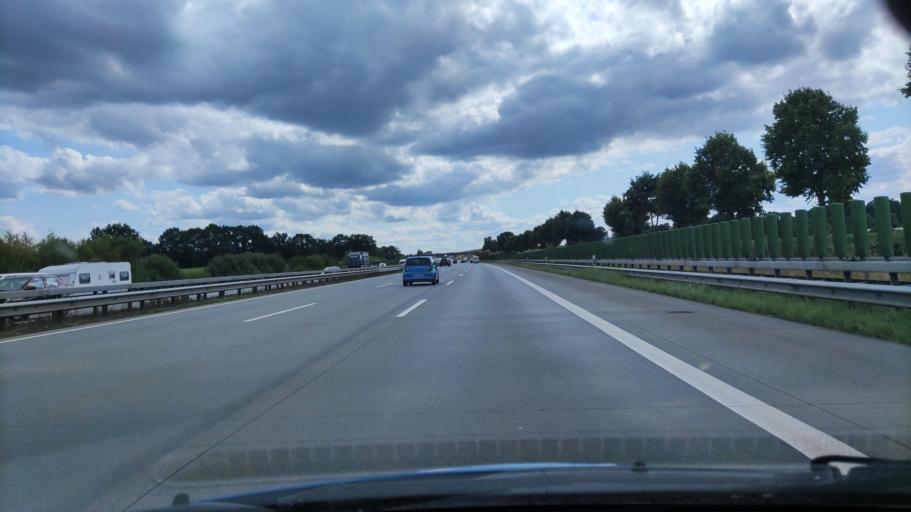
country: DE
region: Lower Saxony
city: Gyhum
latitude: 53.2224
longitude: 9.3235
